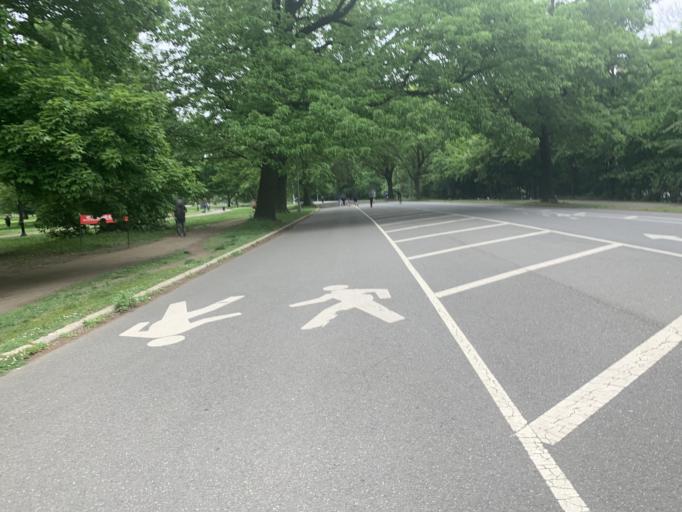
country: US
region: New York
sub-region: Kings County
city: Brooklyn
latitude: 40.6538
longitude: -73.9664
